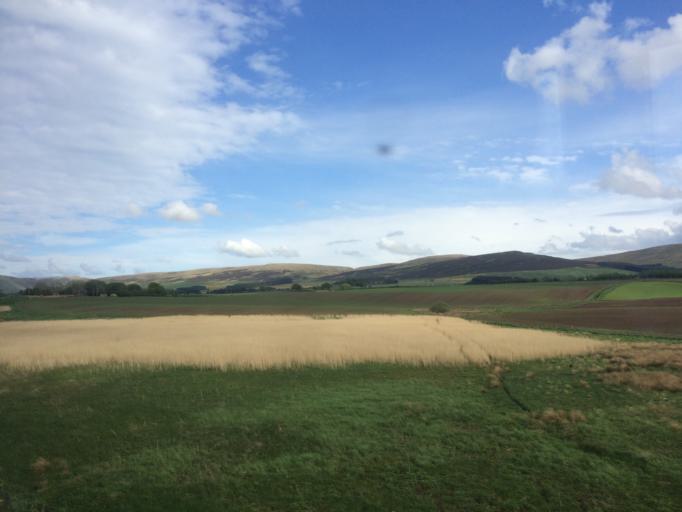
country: GB
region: Scotland
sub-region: Perth and Kinross
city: Auchterarder
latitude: 56.2631
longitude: -3.8090
